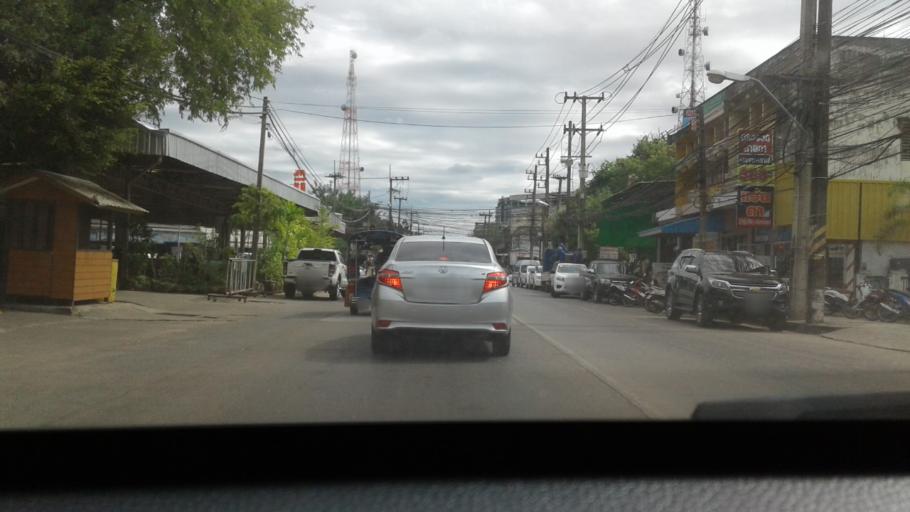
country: TH
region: Changwat Udon Thani
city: Udon Thani
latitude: 17.4140
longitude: 102.7910
